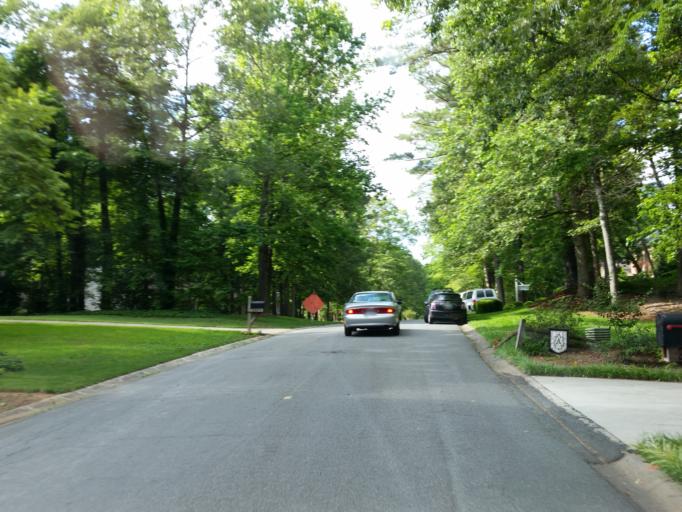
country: US
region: Georgia
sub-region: Fulton County
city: Roswell
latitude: 34.0040
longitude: -84.4189
